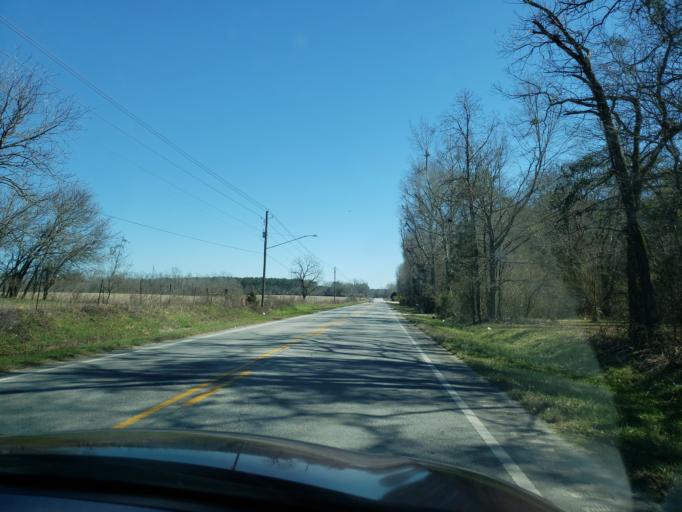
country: US
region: Alabama
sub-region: Lee County
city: Auburn
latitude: 32.6034
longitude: -85.5878
